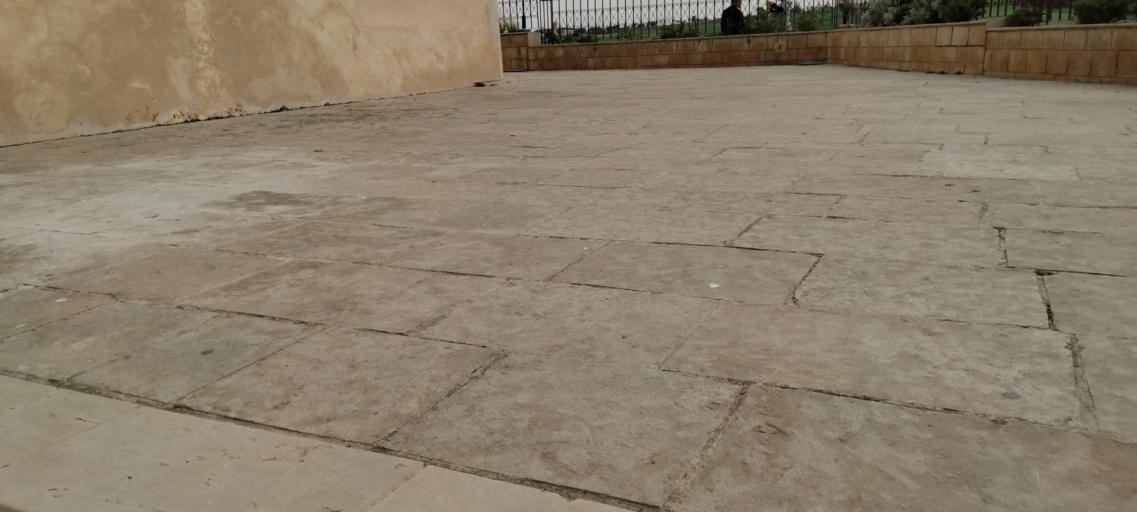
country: MA
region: Fes-Boulemane
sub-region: Fes
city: Fes
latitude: 34.0543
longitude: -4.9705
